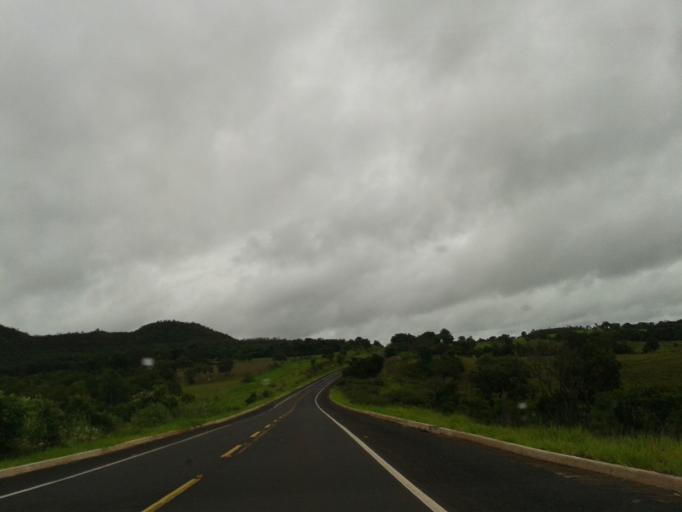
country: BR
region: Minas Gerais
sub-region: Santa Vitoria
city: Santa Vitoria
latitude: -19.1998
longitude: -50.0289
